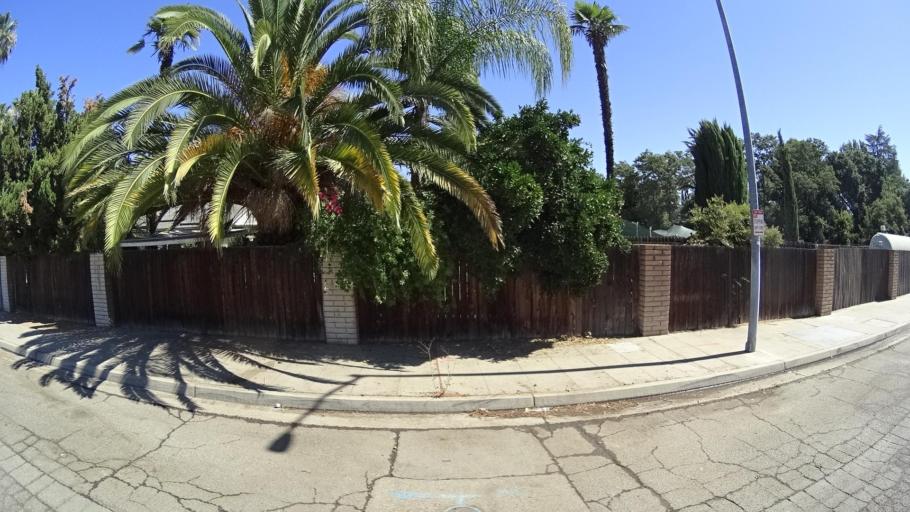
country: US
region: California
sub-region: Fresno County
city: Sunnyside
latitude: 36.7426
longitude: -119.6932
